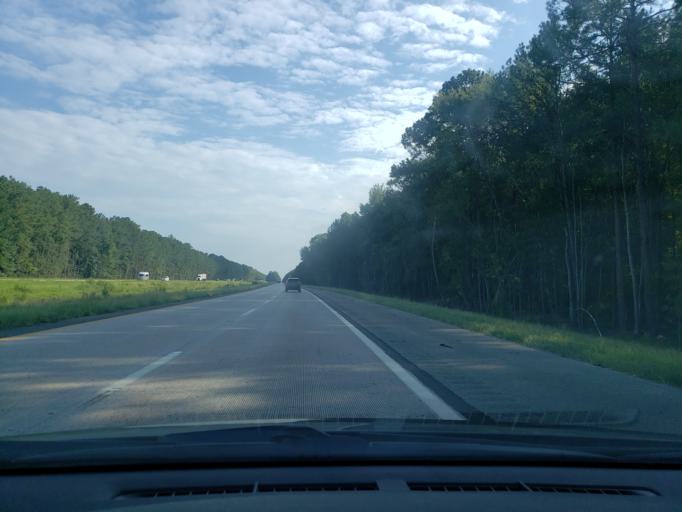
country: US
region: South Carolina
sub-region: Jasper County
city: Ridgeland
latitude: 32.4152
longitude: -81.0122
